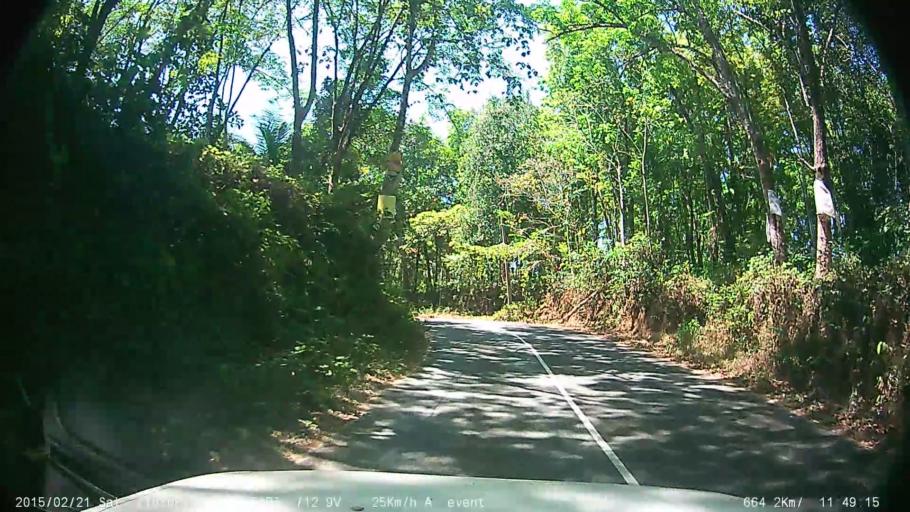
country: IN
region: Kerala
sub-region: Kottayam
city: Lalam
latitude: 9.7694
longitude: 76.7087
